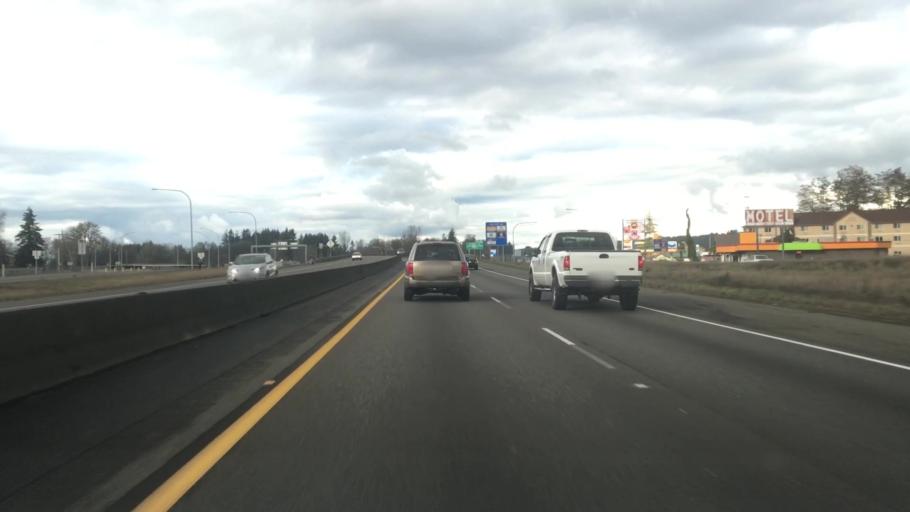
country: US
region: Washington
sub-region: Lewis County
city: Centralia
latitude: 46.7083
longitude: -122.9743
